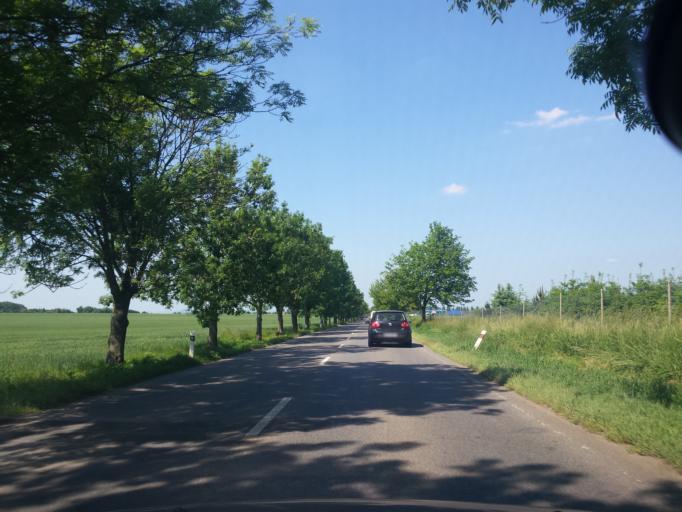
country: CZ
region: Central Bohemia
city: Velke Prilepy
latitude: 50.1734
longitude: 14.3178
